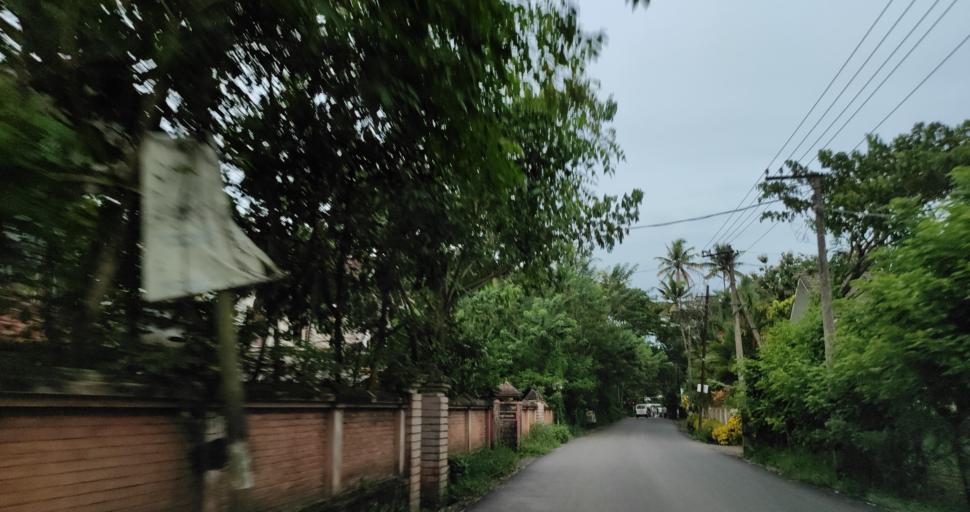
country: IN
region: Kerala
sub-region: Alappuzha
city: Vayalar
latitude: 9.6876
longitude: 76.3285
